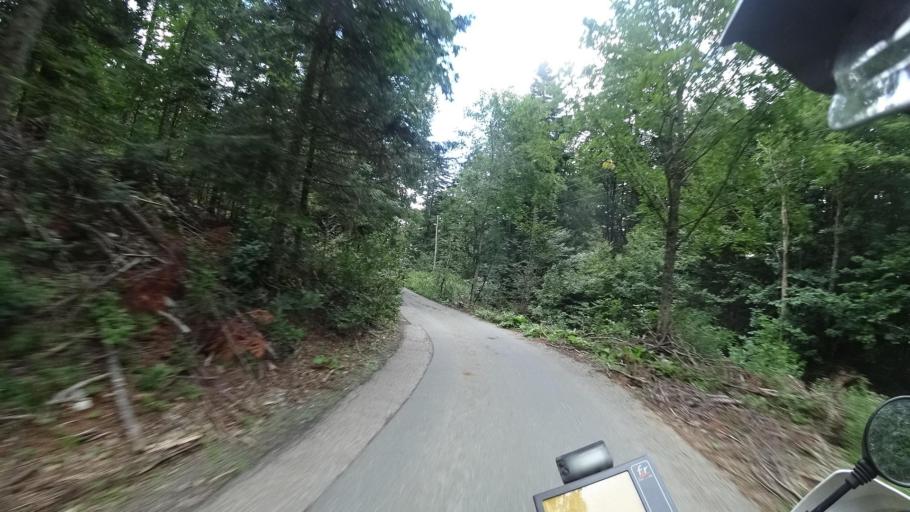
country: HR
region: Licko-Senjska
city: Senj
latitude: 45.1011
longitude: 14.9633
